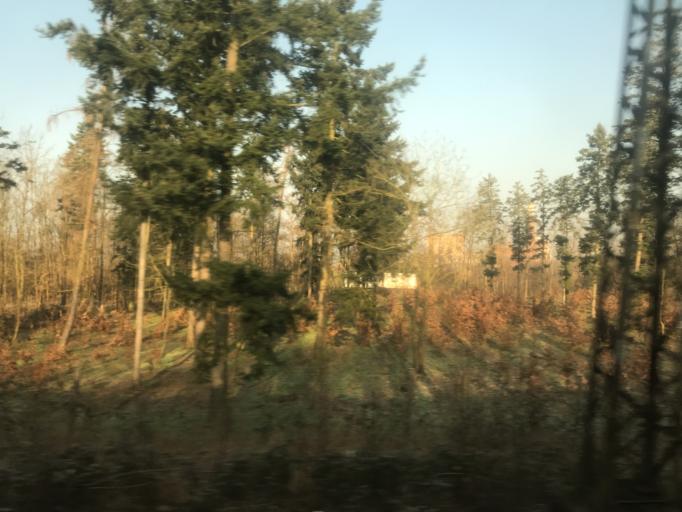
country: DE
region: Hesse
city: Kelsterbach
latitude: 50.0463
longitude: 8.5005
